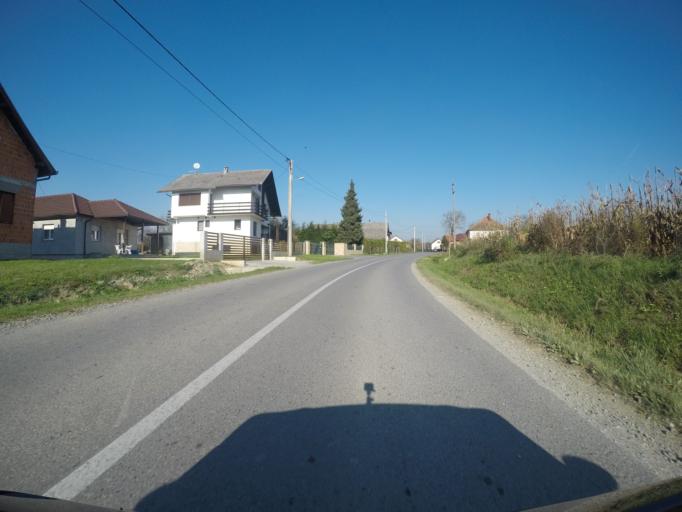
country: HR
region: Bjelovarsko-Bilogorska
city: Predavac
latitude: 45.9197
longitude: 16.7874
